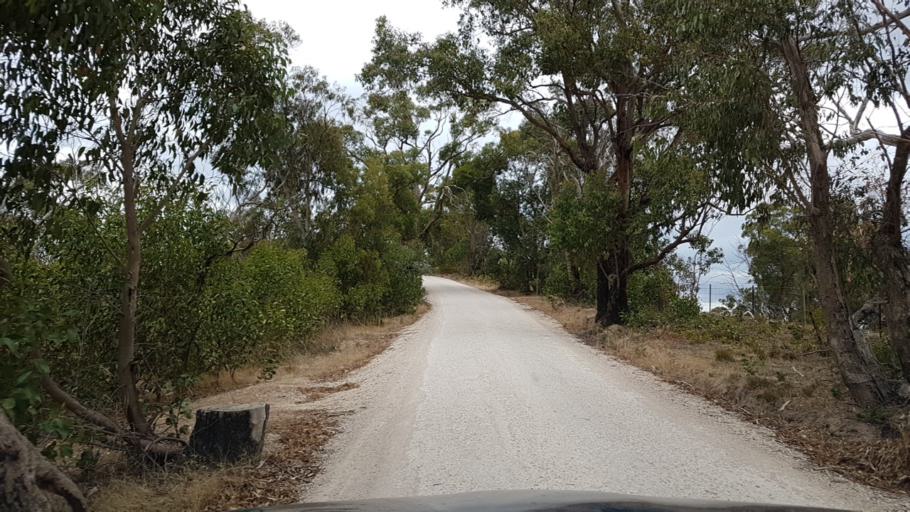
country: AU
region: South Australia
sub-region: Tea Tree Gully
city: Golden Grove
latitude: -34.7751
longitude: 138.8144
